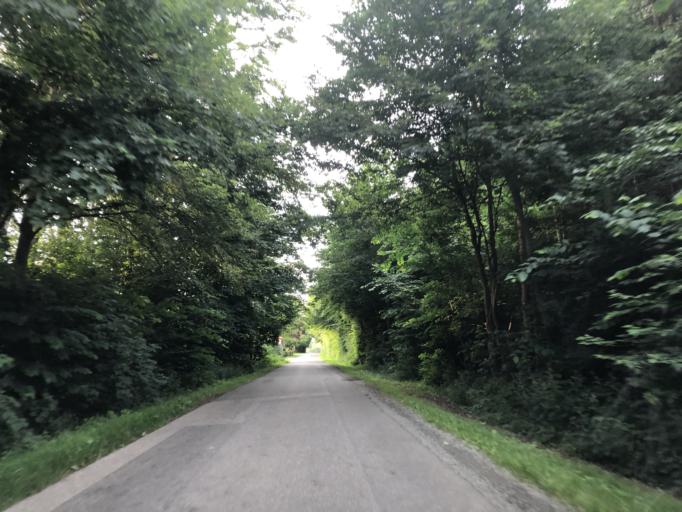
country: DK
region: South Denmark
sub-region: Fredericia Kommune
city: Taulov
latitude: 55.5995
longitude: 9.6020
